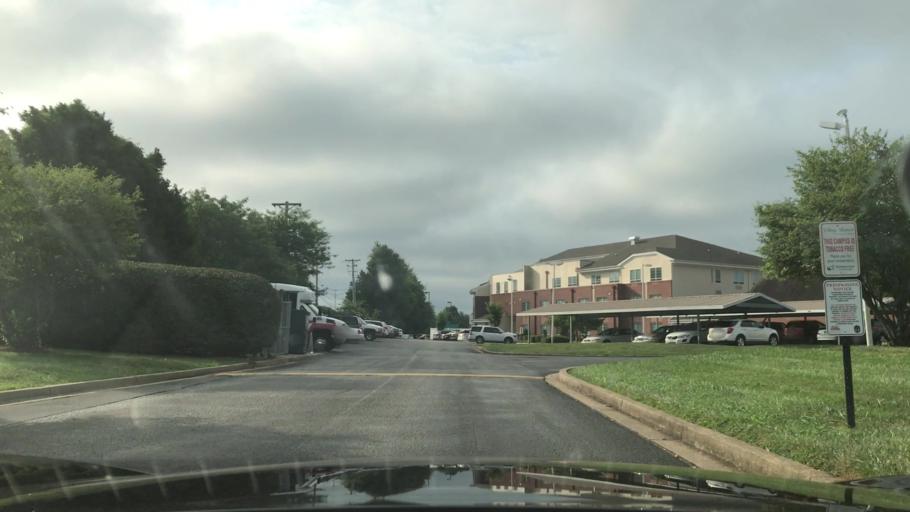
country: US
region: Kentucky
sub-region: Warren County
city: Bowling Green
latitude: 36.9626
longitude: -86.4493
